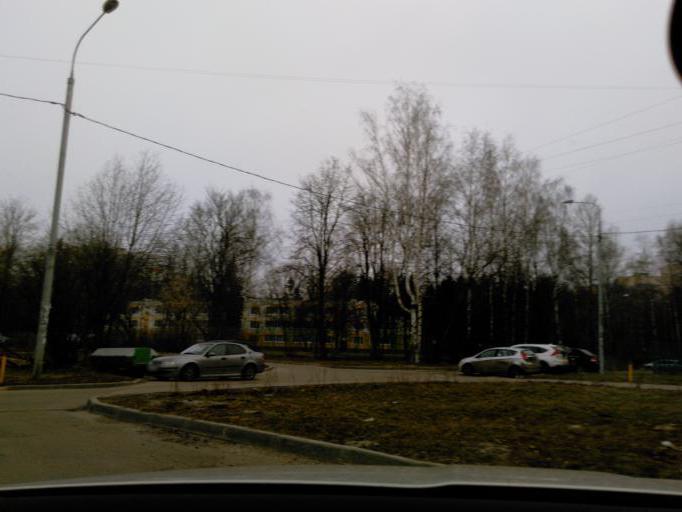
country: RU
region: Moskovskaya
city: Rzhavki
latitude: 55.9938
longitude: 37.2199
